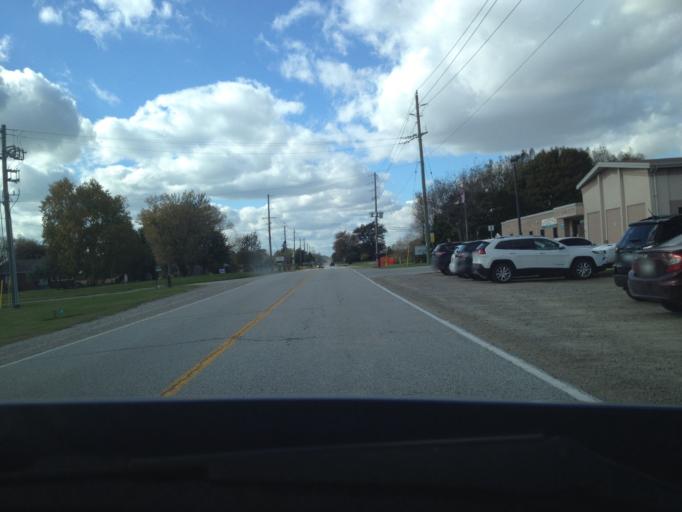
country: CA
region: Ontario
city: Amherstburg
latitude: 42.0325
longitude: -82.5632
